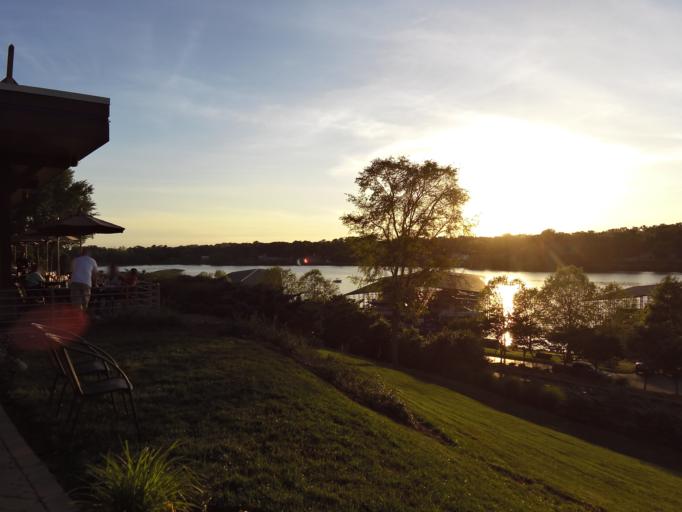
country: US
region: Tennessee
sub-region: Knox County
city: Farragut
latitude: 35.8656
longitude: -84.1300
